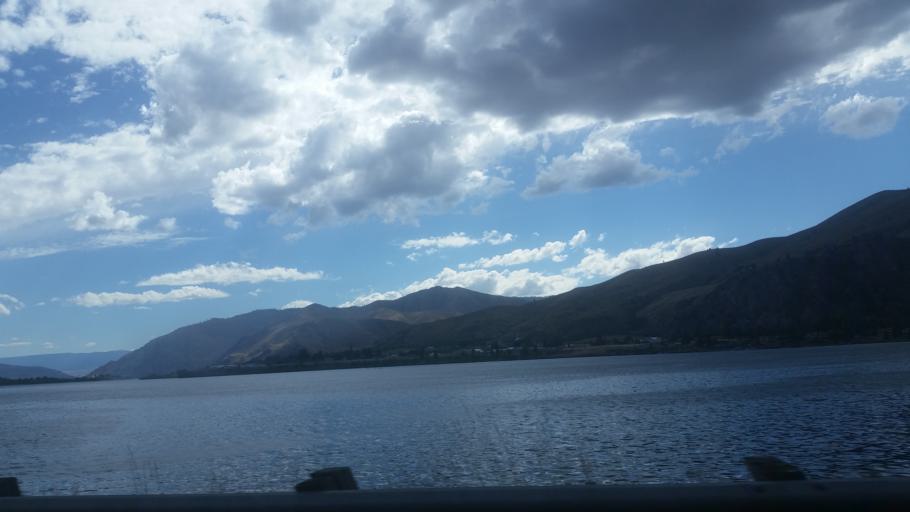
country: US
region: Washington
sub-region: Chelan County
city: Entiat
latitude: 47.6972
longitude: -120.1916
